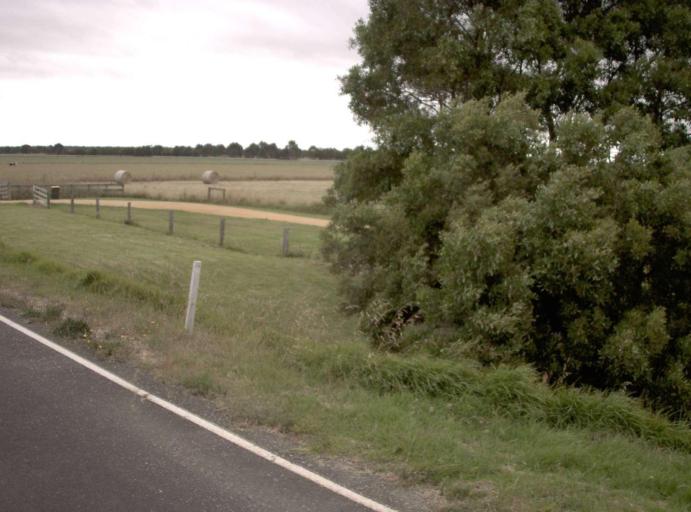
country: AU
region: Victoria
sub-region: Wellington
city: Sale
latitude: -38.5577
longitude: 146.8812
